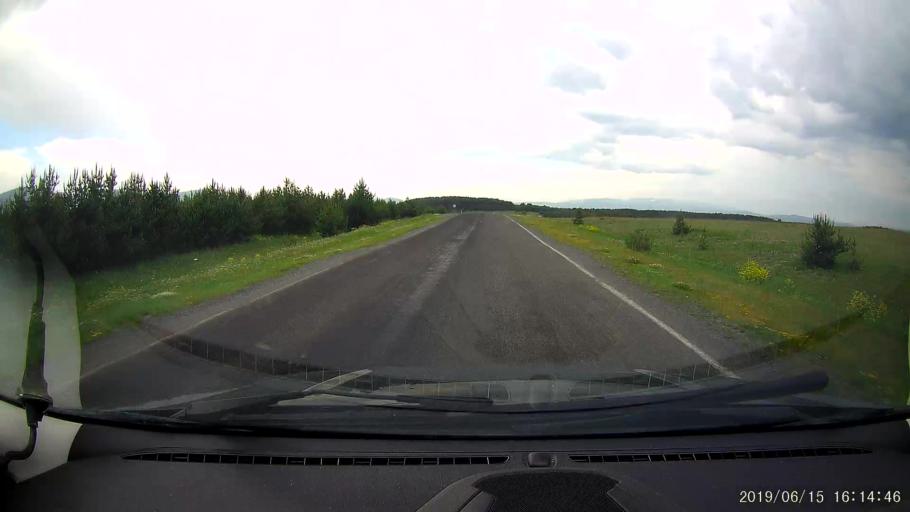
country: TR
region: Ardahan
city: Hanak
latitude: 41.2757
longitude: 42.8482
